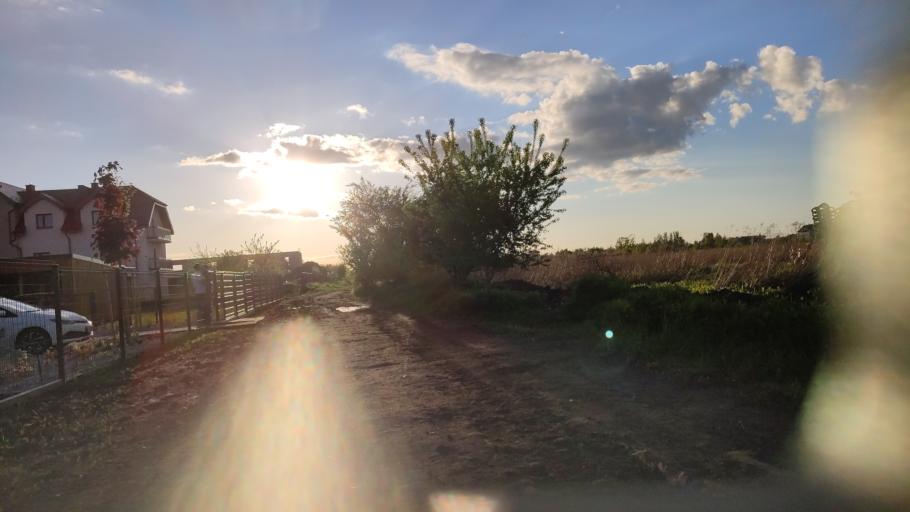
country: PL
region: Lower Silesian Voivodeship
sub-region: Powiat wroclawski
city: Zerniki Wroclawskie
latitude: 51.0481
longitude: 17.0410
